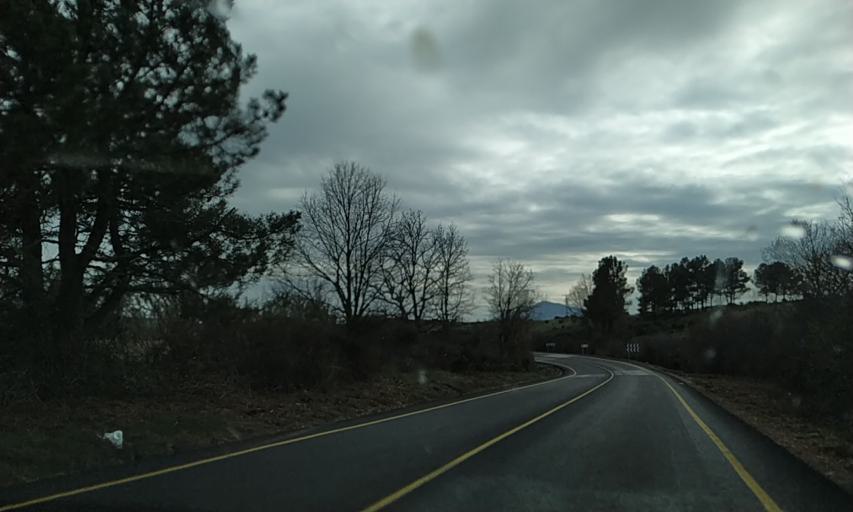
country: ES
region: Castille and Leon
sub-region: Provincia de Salamanca
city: Villasrubias
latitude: 40.3480
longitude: -6.6363
